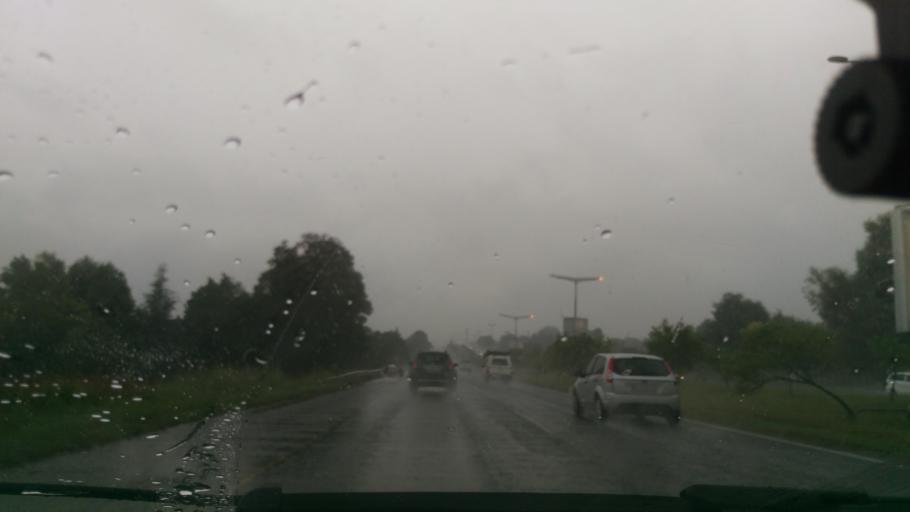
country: ZA
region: Gauteng
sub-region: West Rand District Municipality
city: Muldersdriseloop
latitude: -26.0750
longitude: 27.9356
